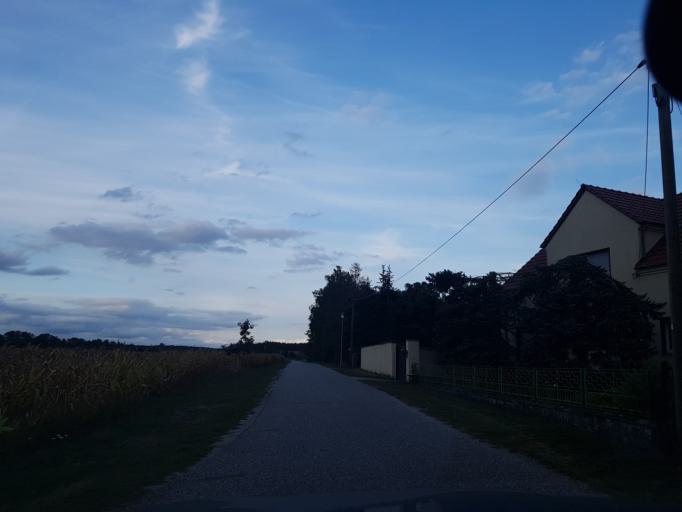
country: DE
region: Brandenburg
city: Schilda
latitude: 51.6330
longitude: 13.3746
